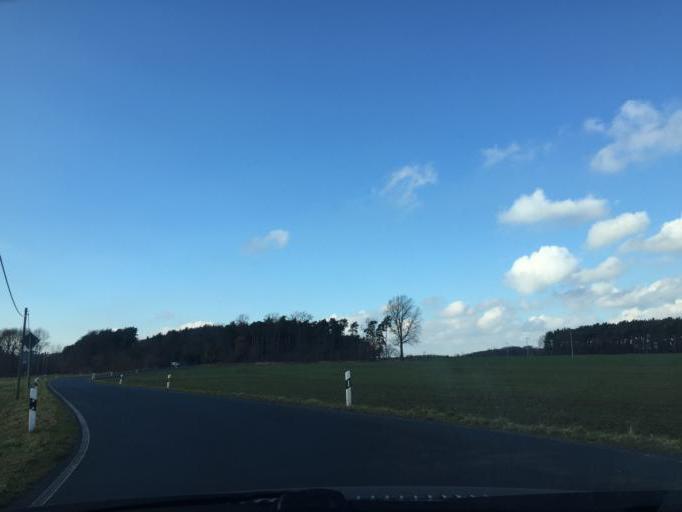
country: DE
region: Saxony
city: Thiendorf
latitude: 51.2811
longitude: 13.7410
